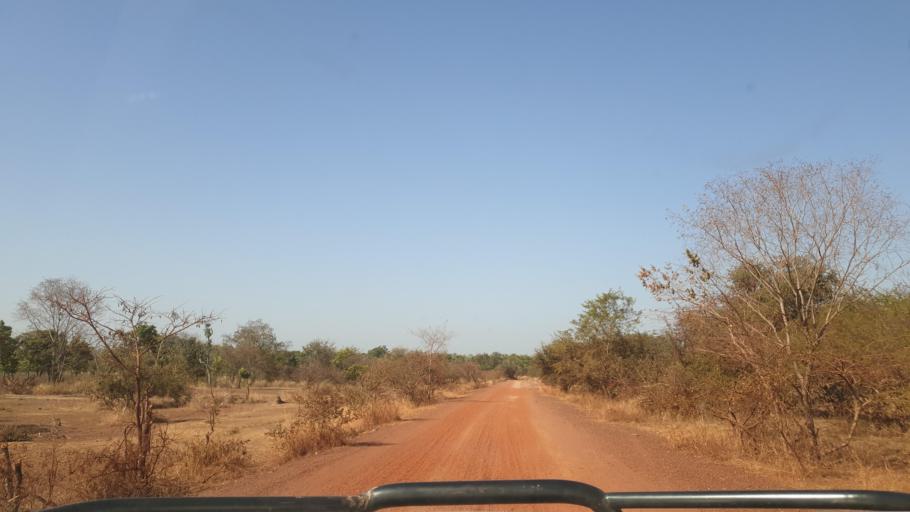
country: ML
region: Sikasso
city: Bougouni
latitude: 11.8207
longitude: -6.9619
